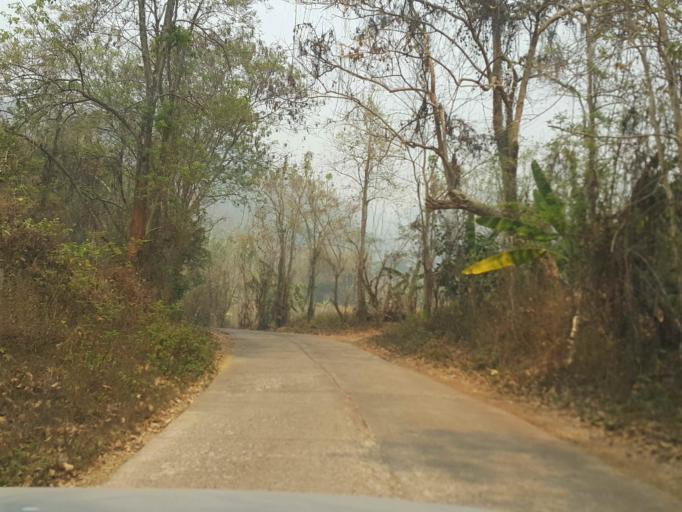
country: TH
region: Chiang Mai
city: Mae Taeng
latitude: 19.2206
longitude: 98.8543
